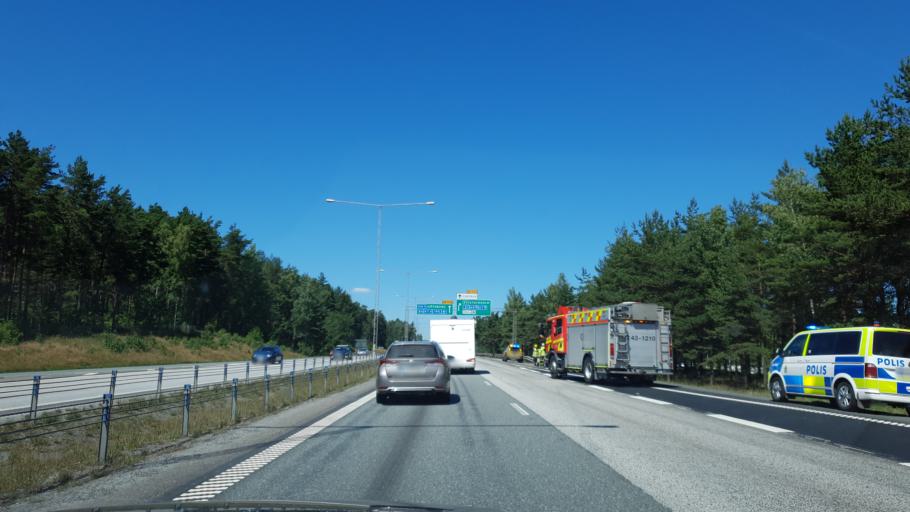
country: SE
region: Joenkoeping
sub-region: Jonkopings Kommun
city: Jonkoping
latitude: 57.7504
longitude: 14.1585
